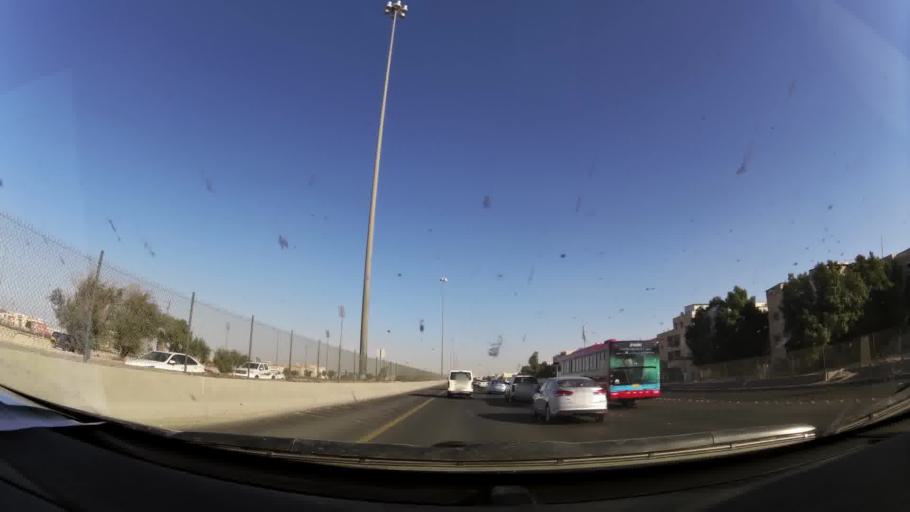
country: KW
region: Al Asimah
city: Ar Rabiyah
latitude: 29.2670
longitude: 47.9202
